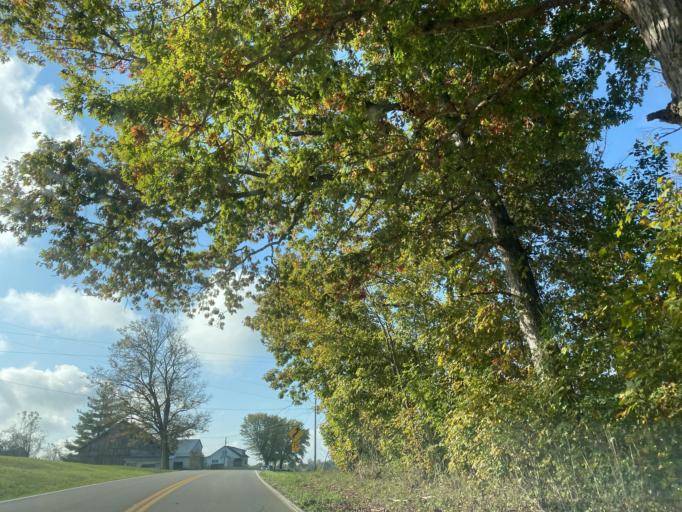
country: US
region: Kentucky
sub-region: Pendleton County
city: Falmouth
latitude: 38.6967
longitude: -84.3042
